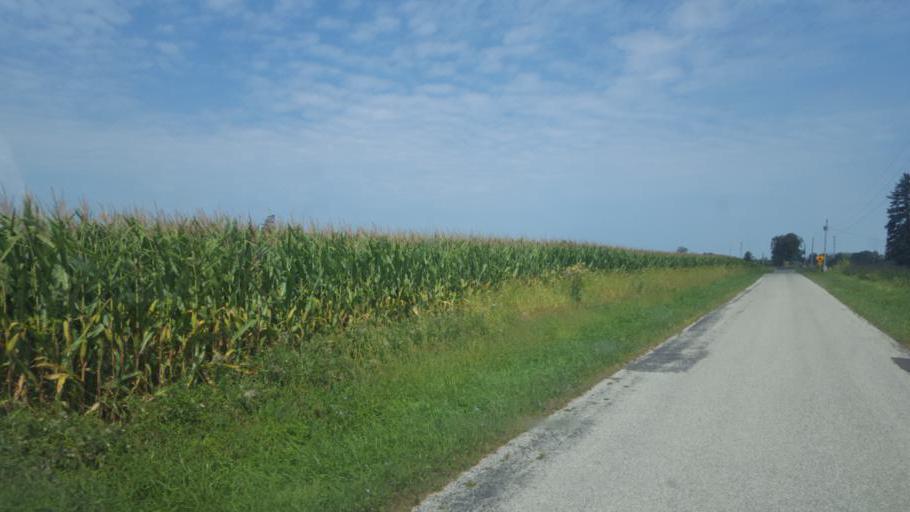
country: US
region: Ohio
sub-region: Delaware County
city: Ashley
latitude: 40.4928
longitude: -83.0391
